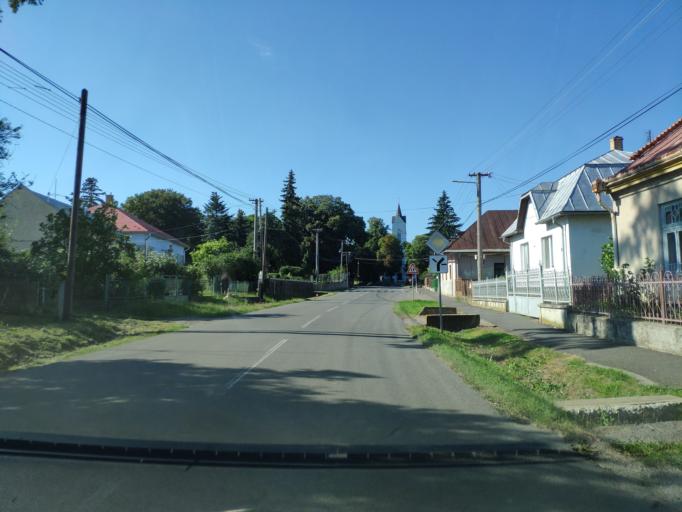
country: SK
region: Kosicky
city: Trebisov
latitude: 48.5804
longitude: 21.8496
